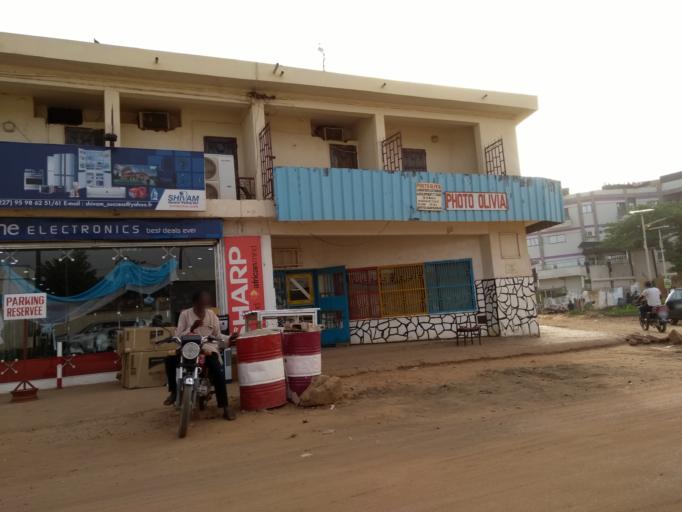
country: NE
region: Niamey
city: Niamey
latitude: 13.5154
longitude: 2.1127
